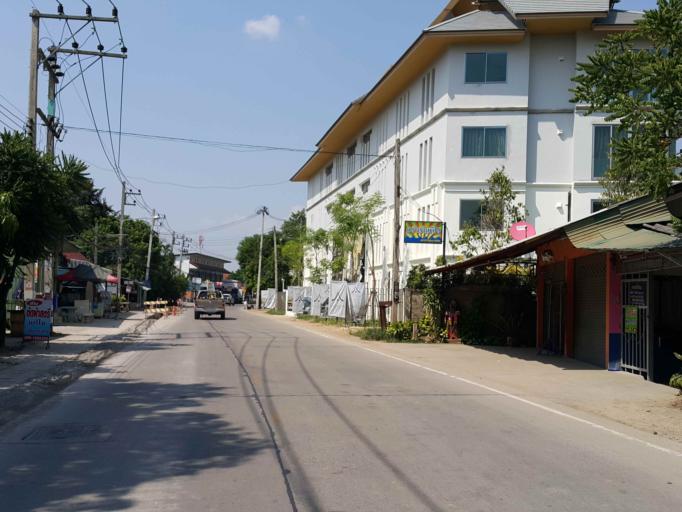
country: TH
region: Chiang Mai
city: Chiang Mai
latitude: 18.7471
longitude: 98.9851
